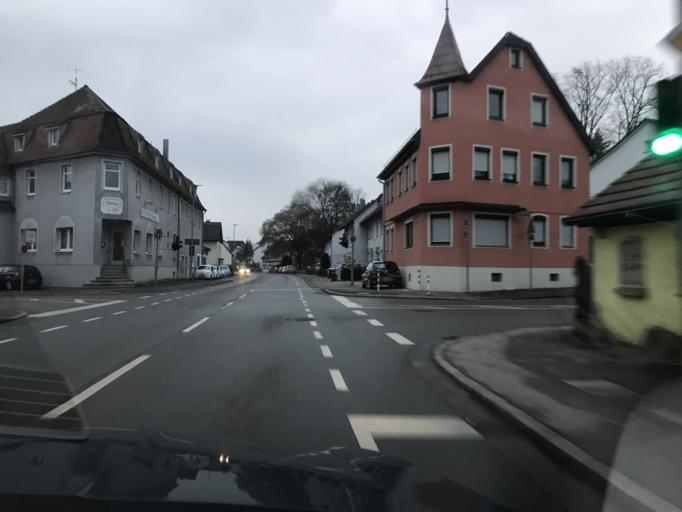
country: DE
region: Baden-Wuerttemberg
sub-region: Regierungsbezirk Stuttgart
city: Kongen
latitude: 48.6820
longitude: 9.3695
